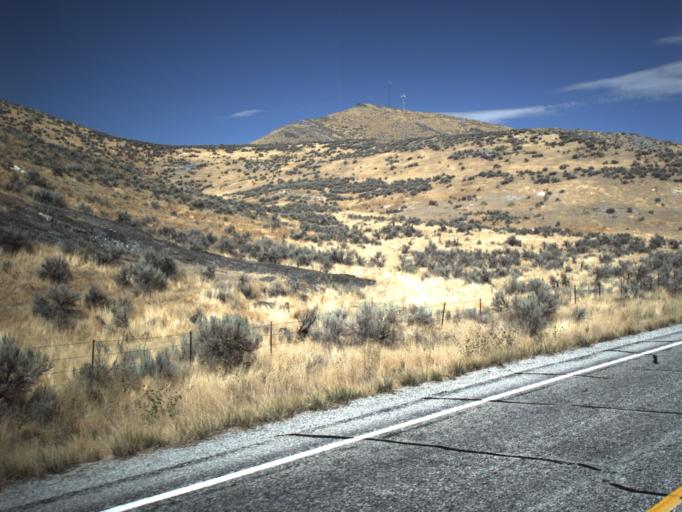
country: US
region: Utah
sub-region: Box Elder County
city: Tremonton
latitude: 41.6800
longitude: -112.4441
